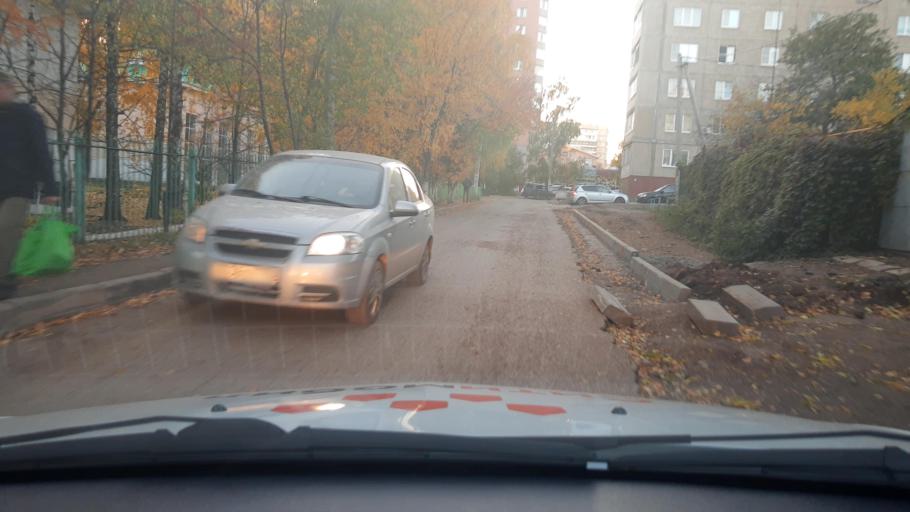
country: RU
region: Bashkortostan
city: Ufa
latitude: 54.7059
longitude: 56.0034
